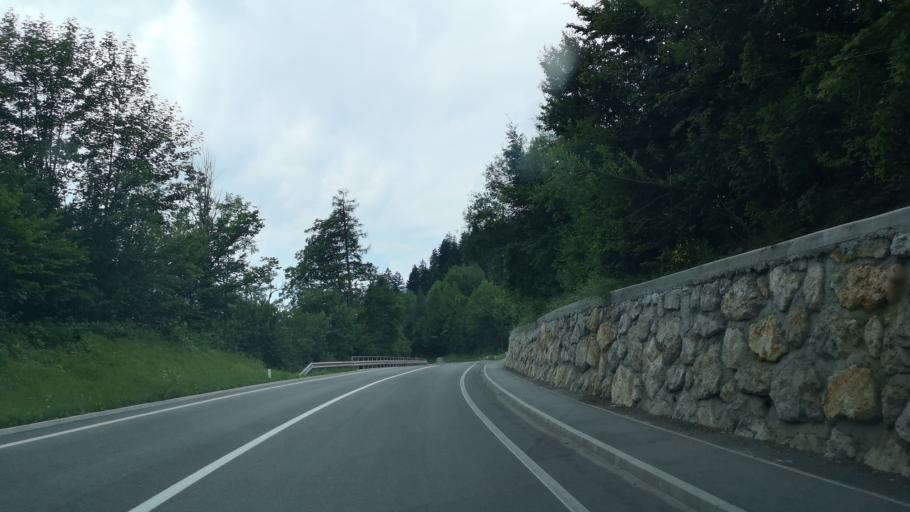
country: SI
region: Jesenice
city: Hrusica
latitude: 46.4440
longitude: 14.0320
